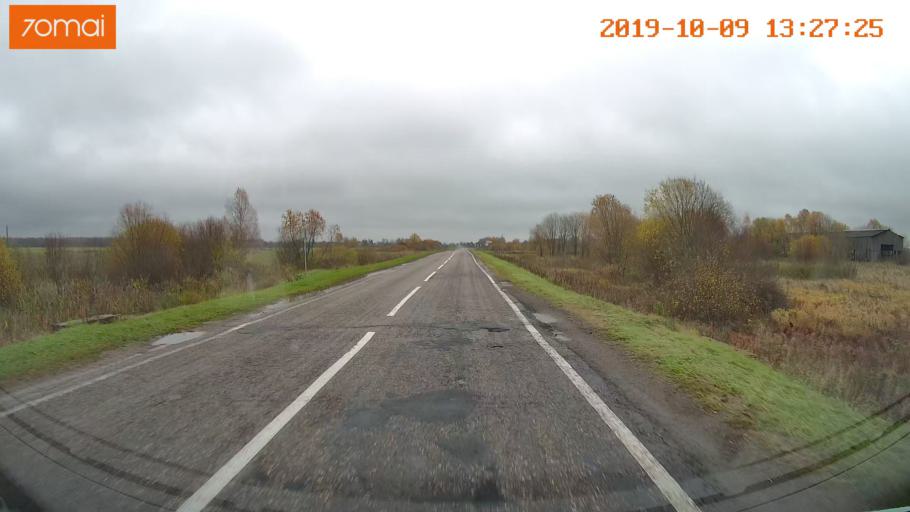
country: RU
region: Jaroslavl
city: Lyubim
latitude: 58.3156
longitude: 40.9472
